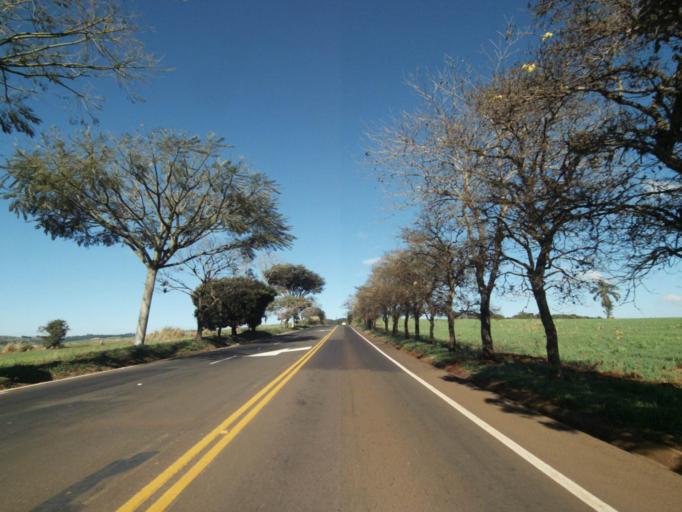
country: BR
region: Parana
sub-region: Londrina
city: Londrina
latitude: -23.6628
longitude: -51.1158
